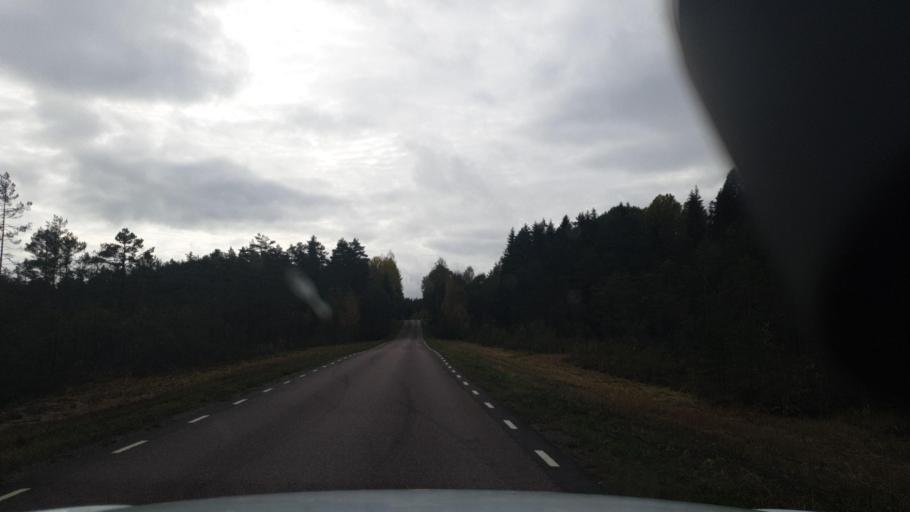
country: SE
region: Vaermland
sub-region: Karlstads Kommun
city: Edsvalla
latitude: 59.5180
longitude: 13.1113
